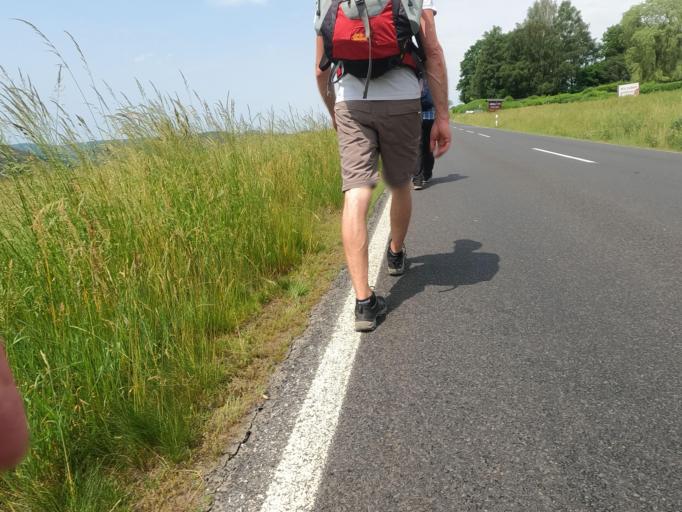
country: DE
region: Rheinland-Pfalz
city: Unnau
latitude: 50.6396
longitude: 7.9021
